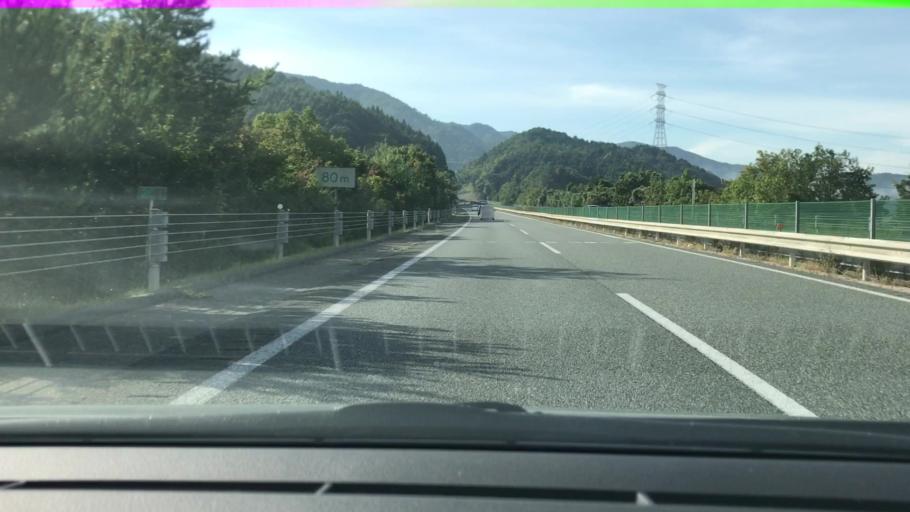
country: JP
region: Hyogo
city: Sasayama
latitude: 35.0468
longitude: 135.1825
